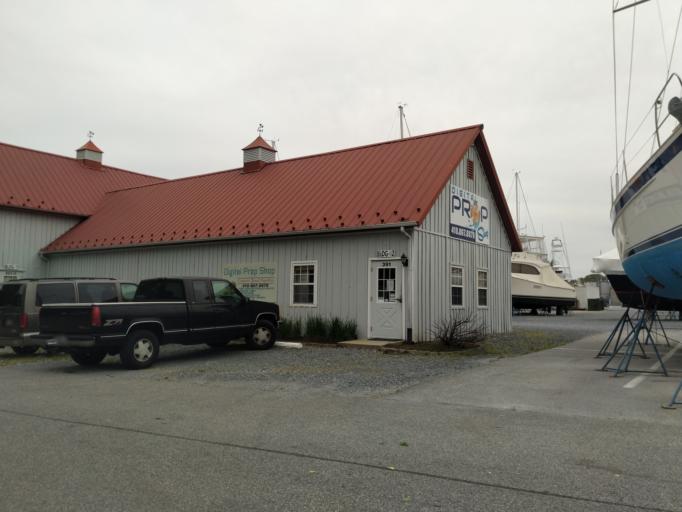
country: US
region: Maryland
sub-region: Anne Arundel County
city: Deale
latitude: 38.7769
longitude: -76.5659
